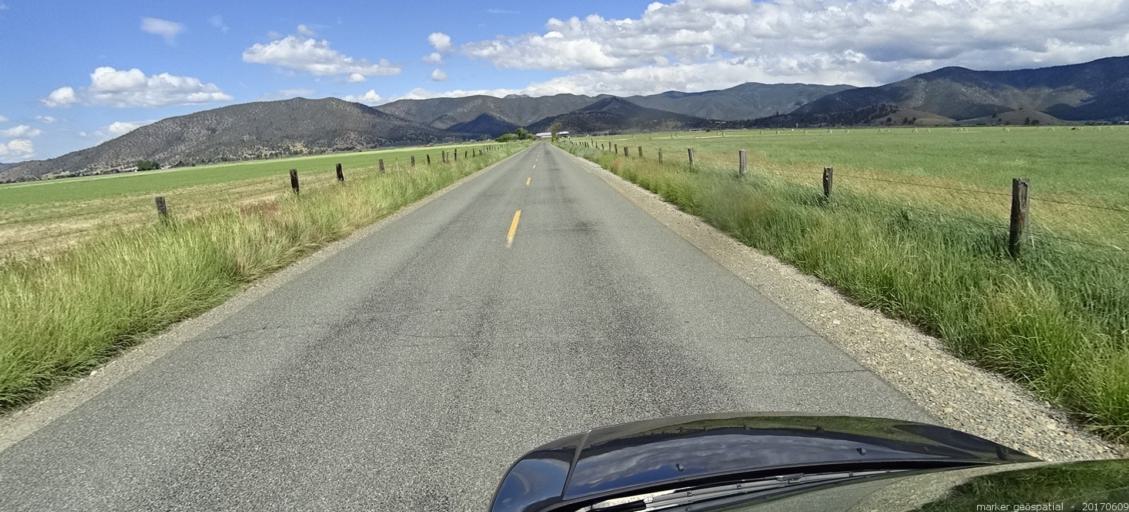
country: US
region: California
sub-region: Siskiyou County
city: Yreka
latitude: 41.4889
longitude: -122.8677
